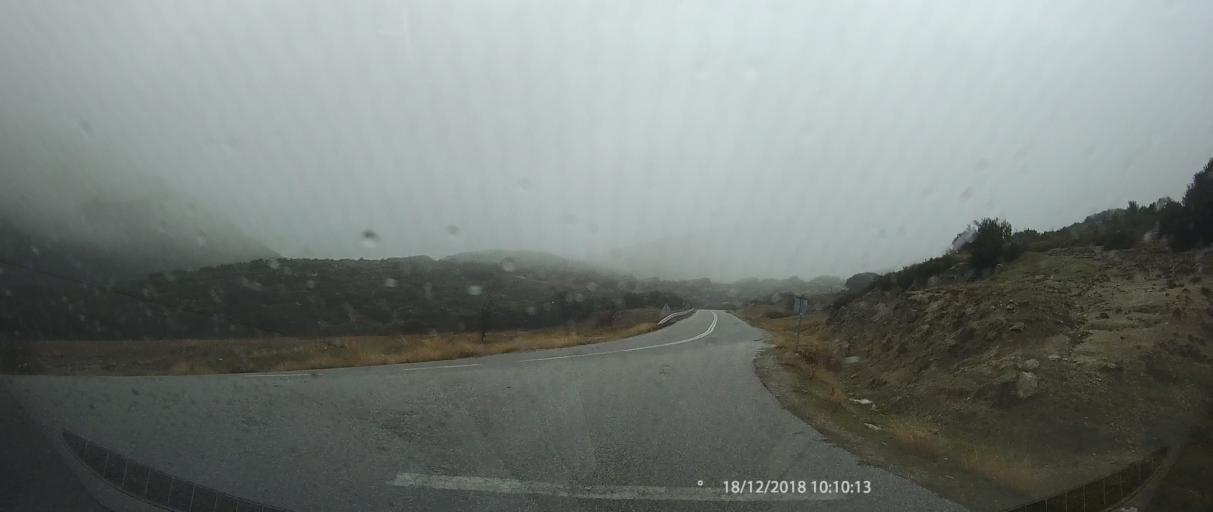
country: GR
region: Thessaly
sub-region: Nomos Larisis
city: Livadi
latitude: 40.0877
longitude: 22.2128
